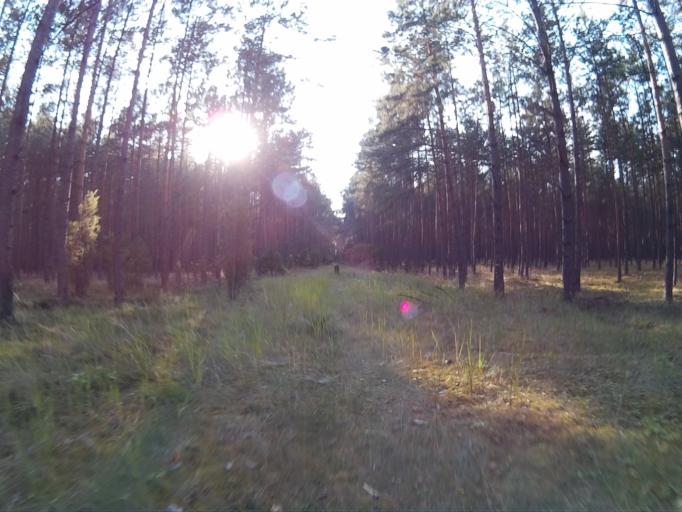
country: PL
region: Kujawsko-Pomorskie
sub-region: Powiat tucholski
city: Cekcyn
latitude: 53.5512
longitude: 18.1072
